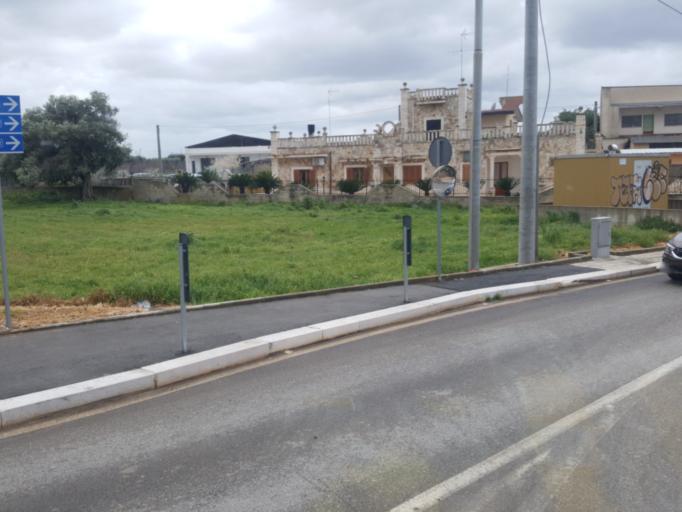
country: IT
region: Apulia
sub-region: Provincia di Bari
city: Turi
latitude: 40.9205
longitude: 17.0114
